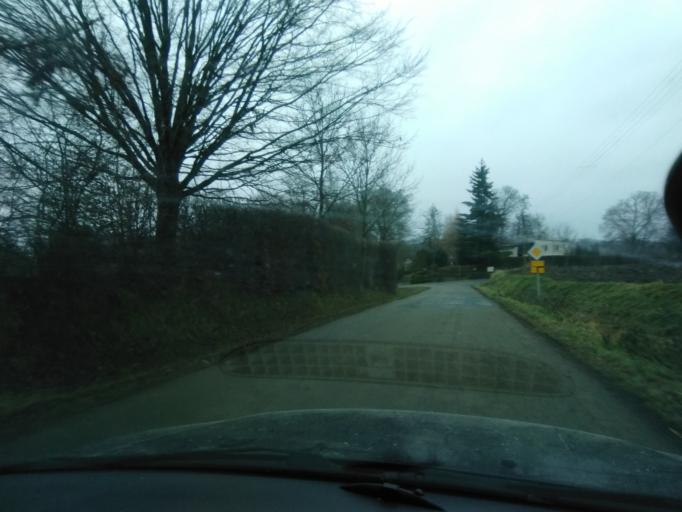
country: PL
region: Subcarpathian Voivodeship
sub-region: Powiat jaroslawski
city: Pruchnik
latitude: 49.9312
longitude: 22.5356
